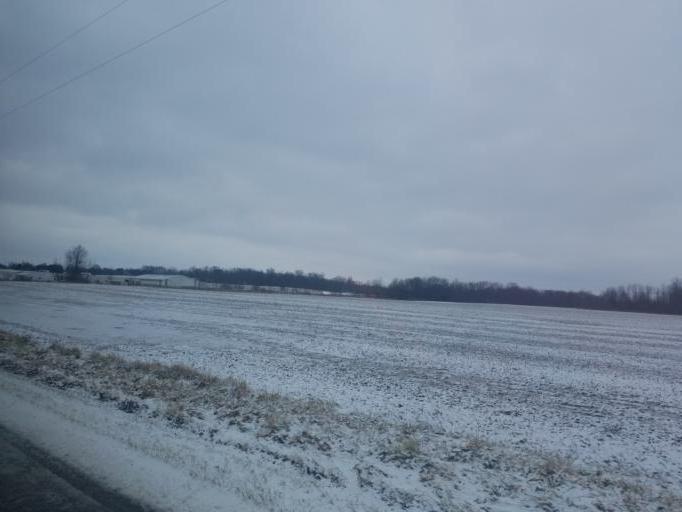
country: US
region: Ohio
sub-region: Delaware County
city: Sunbury
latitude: 40.2216
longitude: -82.7696
